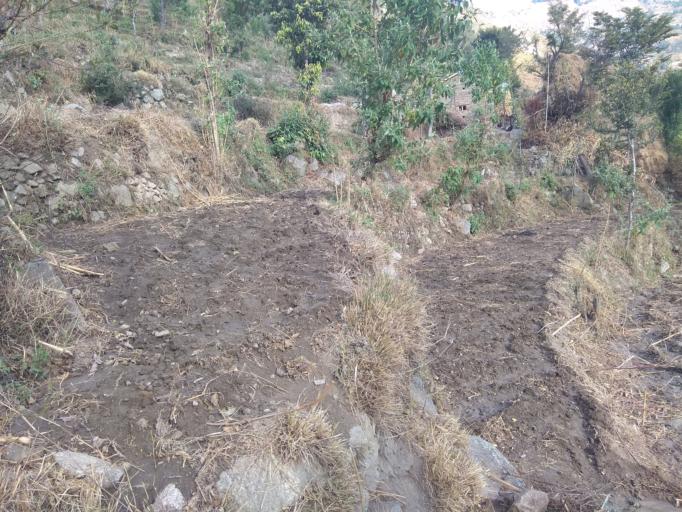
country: NP
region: Mid Western
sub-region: Bheri Zone
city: Dailekh
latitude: 29.2339
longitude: 81.6493
